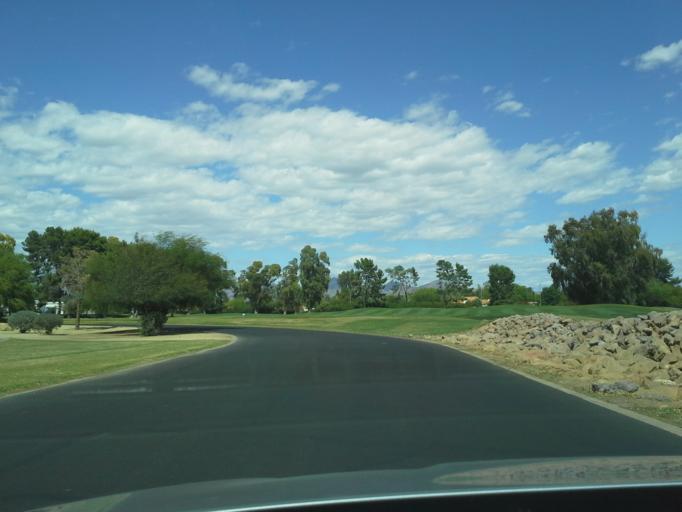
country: US
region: Arizona
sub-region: Maricopa County
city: Paradise Valley
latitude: 33.5546
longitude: -111.9285
